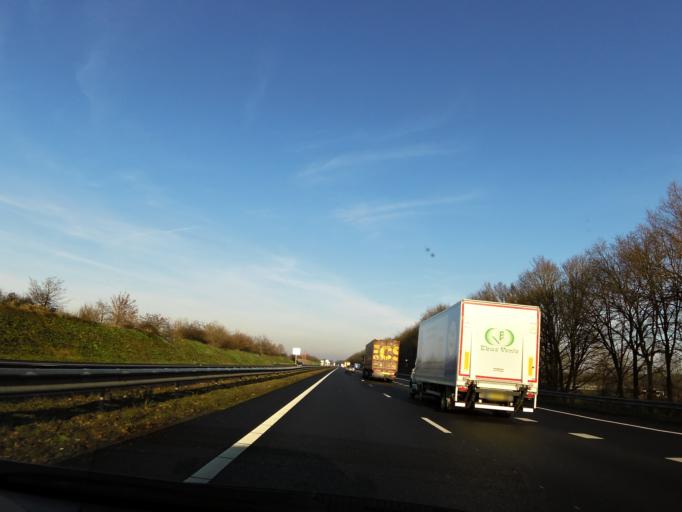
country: NL
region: Limburg
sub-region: Gemeente Peel en Maas
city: Maasbree
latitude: 51.4530
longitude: 6.0661
